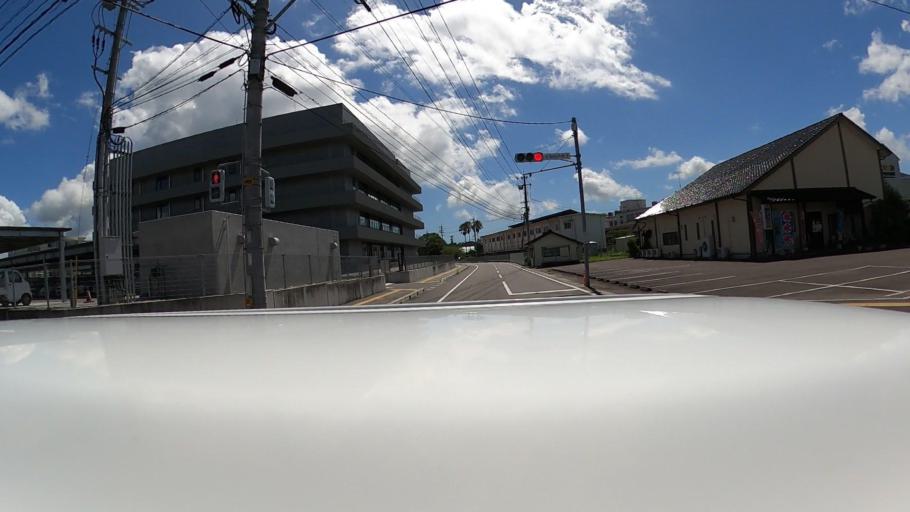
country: JP
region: Miyazaki
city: Tsuma
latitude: 32.1076
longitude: 131.4002
